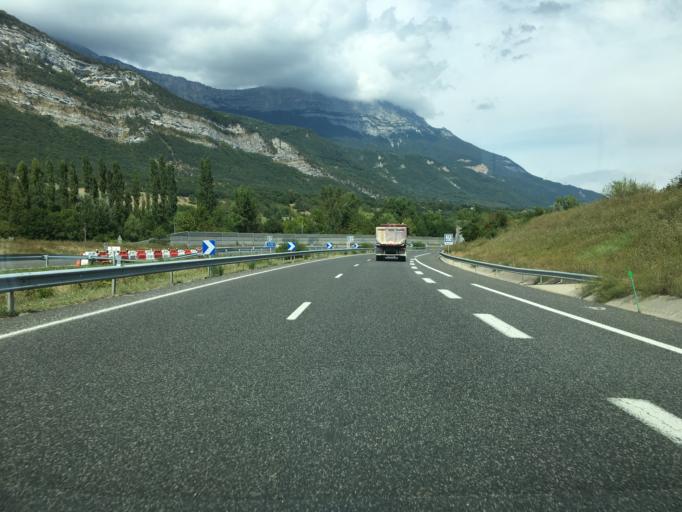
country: FR
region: Rhone-Alpes
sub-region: Departement de l'Isere
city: Allieres-et-Risset
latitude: 45.0882
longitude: 5.6697
